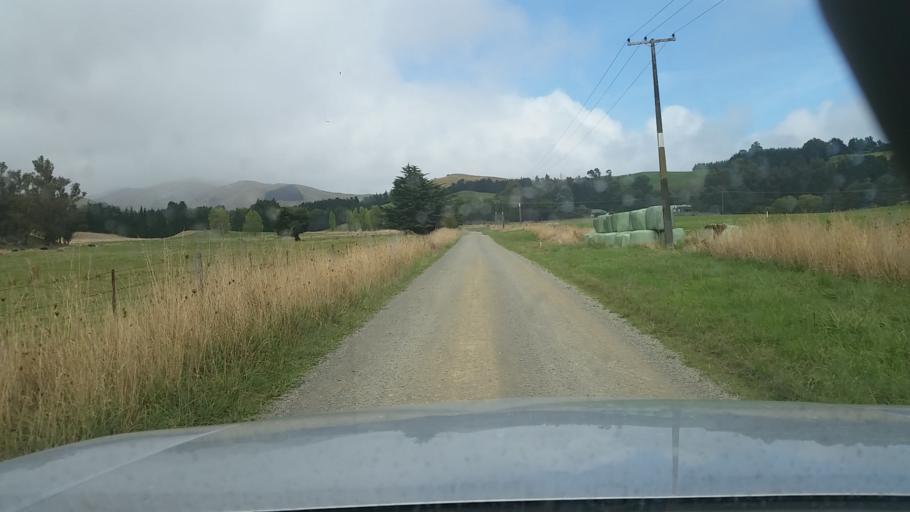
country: NZ
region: Marlborough
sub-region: Marlborough District
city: Blenheim
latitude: -41.7262
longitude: 173.9246
